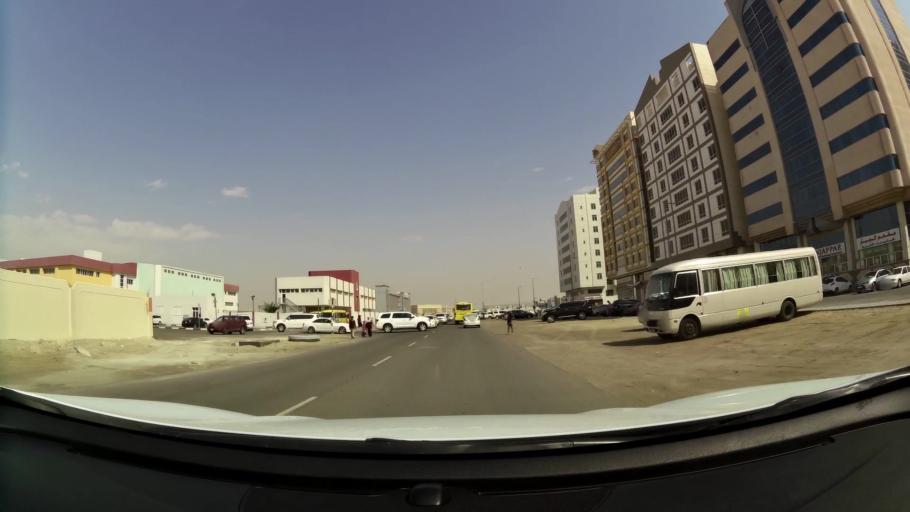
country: AE
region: Abu Dhabi
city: Abu Dhabi
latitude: 24.3451
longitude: 54.5359
